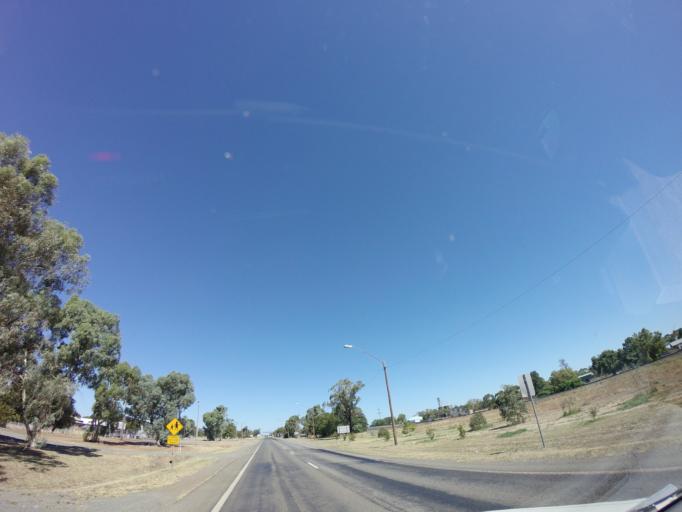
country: AU
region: New South Wales
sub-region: Bogan
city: Nyngan
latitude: -31.5662
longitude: 147.2049
